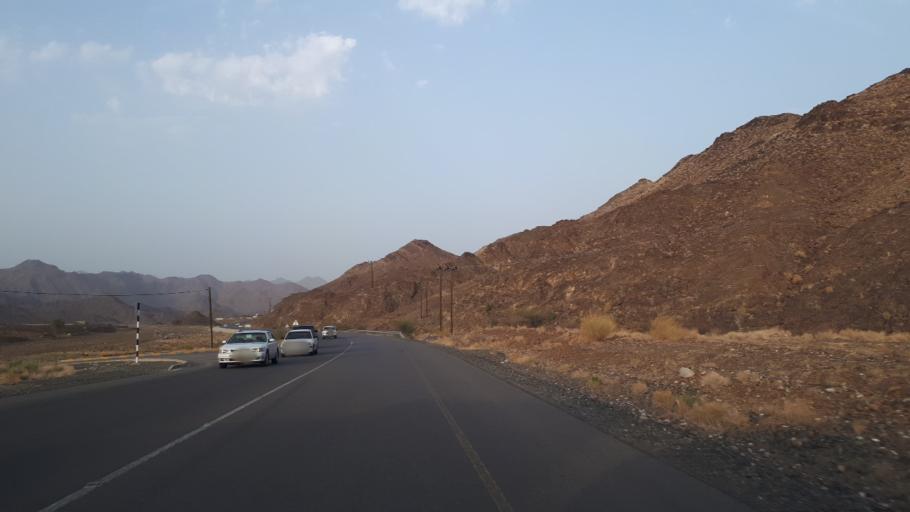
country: OM
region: Al Batinah
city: Rustaq
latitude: 23.4267
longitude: 57.2627
